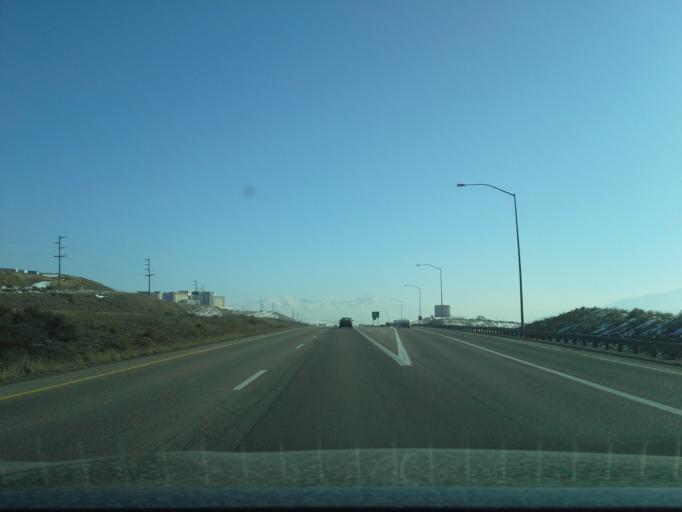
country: US
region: Idaho
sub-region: Bannock County
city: Pocatello
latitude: 42.8822
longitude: -112.4285
